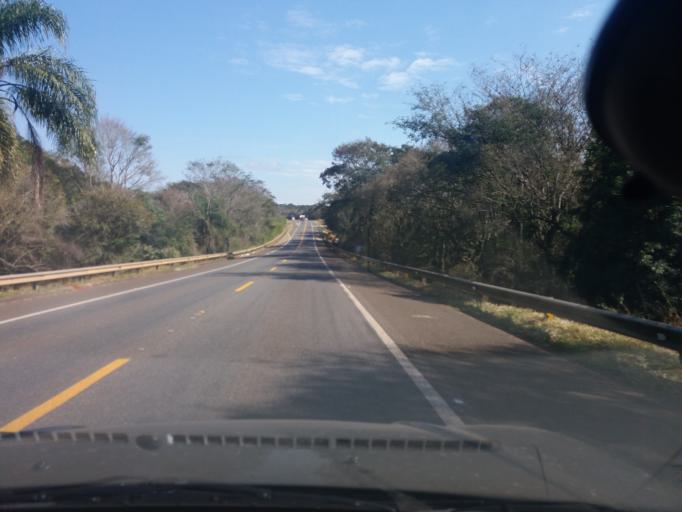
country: BR
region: Sao Paulo
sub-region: Capao Bonito
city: Capao Bonito
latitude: -23.9590
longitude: -48.4584
